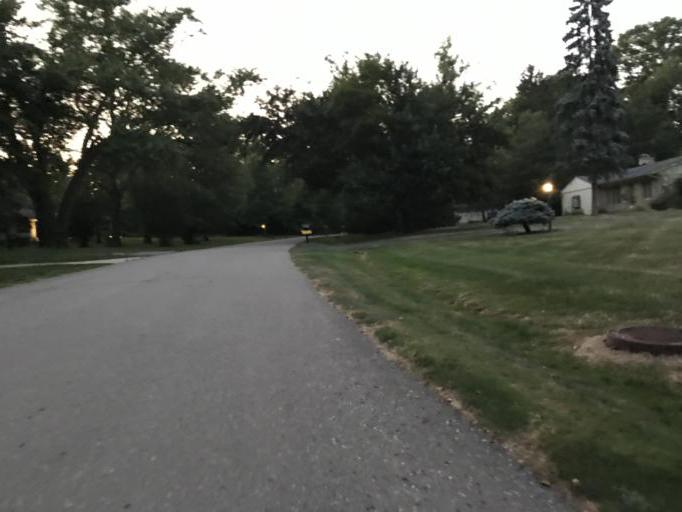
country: US
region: Michigan
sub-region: Oakland County
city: Farmington Hills
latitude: 42.4898
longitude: -83.3541
